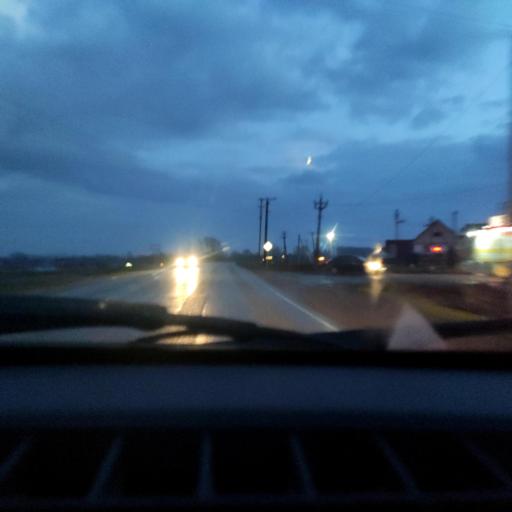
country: RU
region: Bashkortostan
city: Avdon
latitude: 54.7399
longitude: 55.7997
